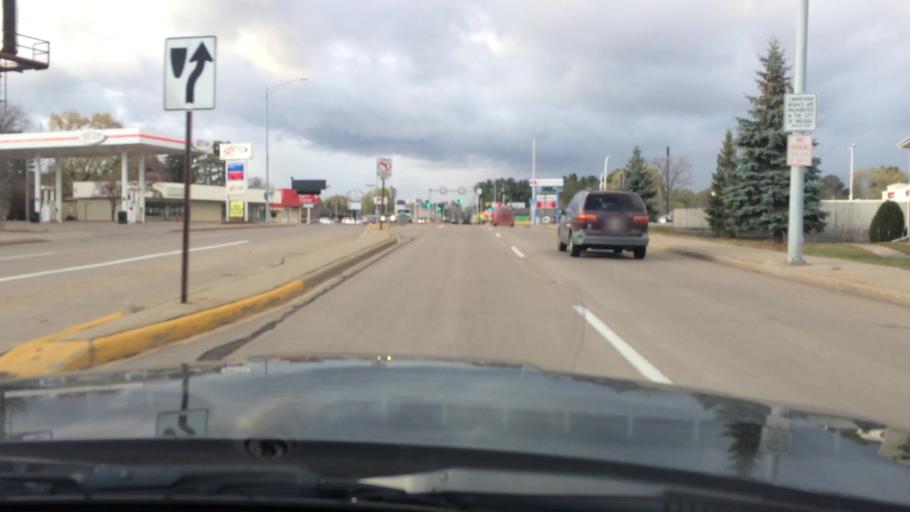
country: US
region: Wisconsin
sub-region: Marathon County
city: Schofield
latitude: 44.9327
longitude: -89.6155
